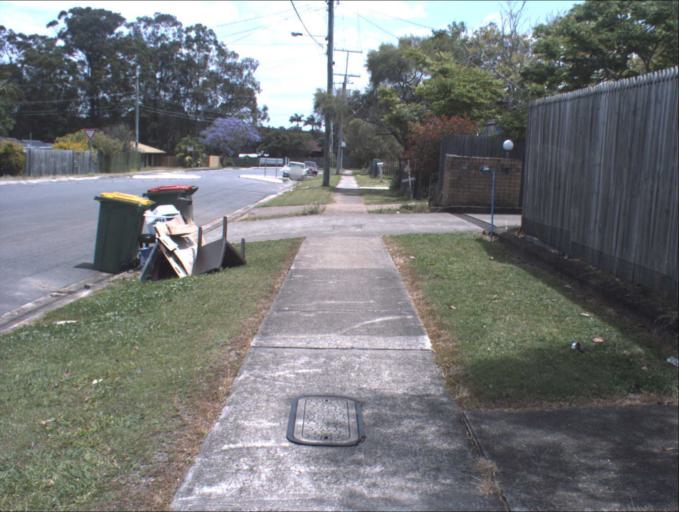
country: AU
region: Queensland
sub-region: Logan
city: Woodridge
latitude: -27.6368
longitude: 153.1000
